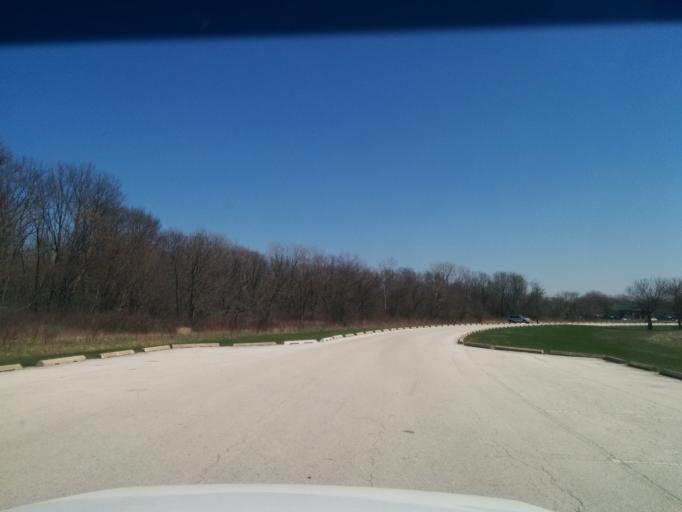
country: US
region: Illinois
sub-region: Cook County
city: Midlothian
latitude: 41.6085
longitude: -87.7219
